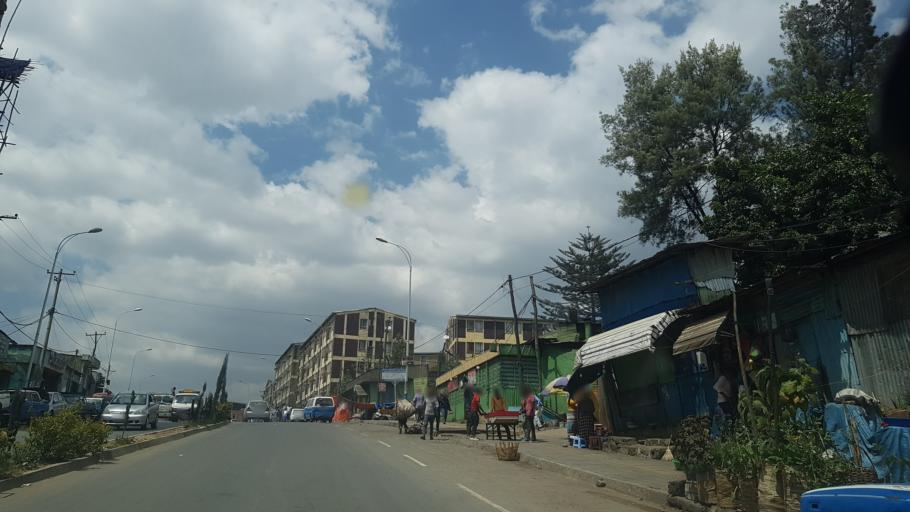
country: ET
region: Adis Abeba
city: Addis Ababa
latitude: 9.0283
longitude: 38.7469
